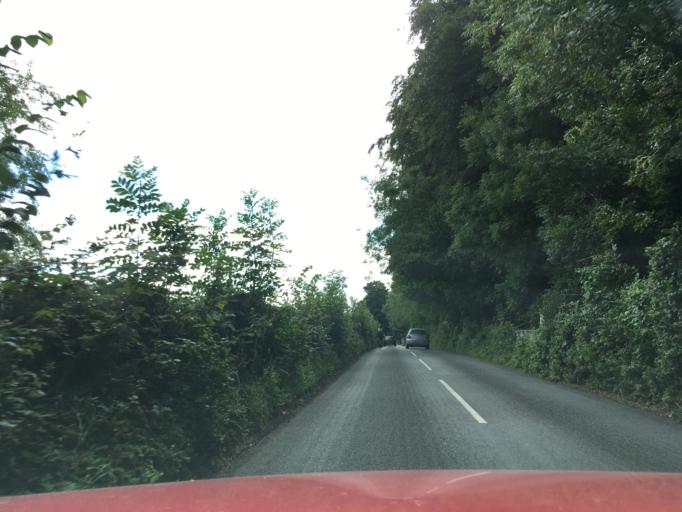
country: GB
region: England
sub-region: Wiltshire
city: Colerne
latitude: 51.4572
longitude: -2.2555
